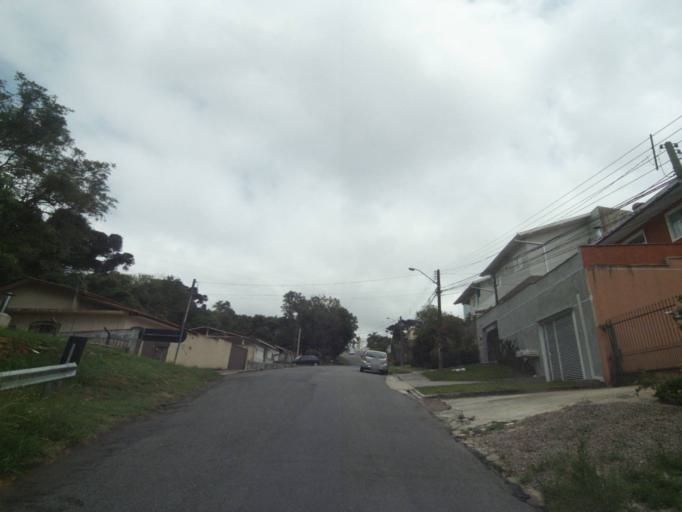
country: BR
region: Parana
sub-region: Curitiba
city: Curitiba
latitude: -25.3903
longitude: -49.2797
